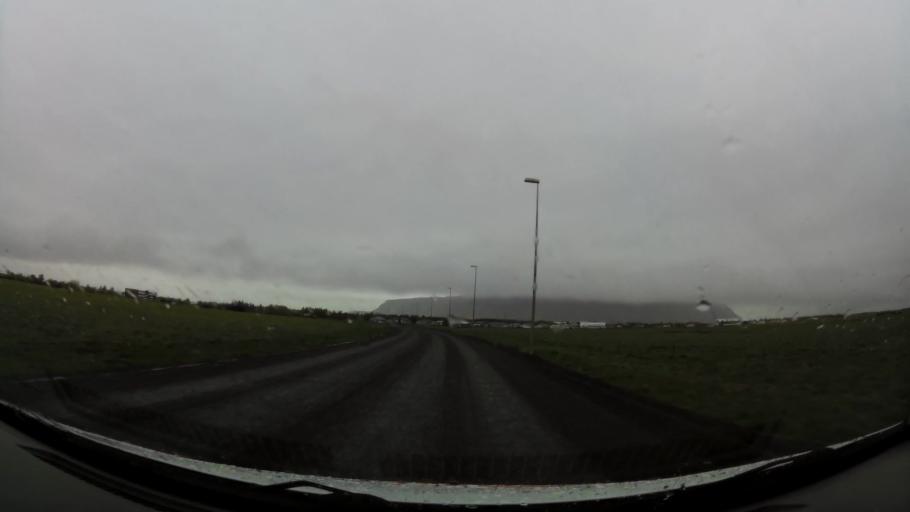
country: IS
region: South
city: Selfoss
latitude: 63.9292
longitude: -20.9709
